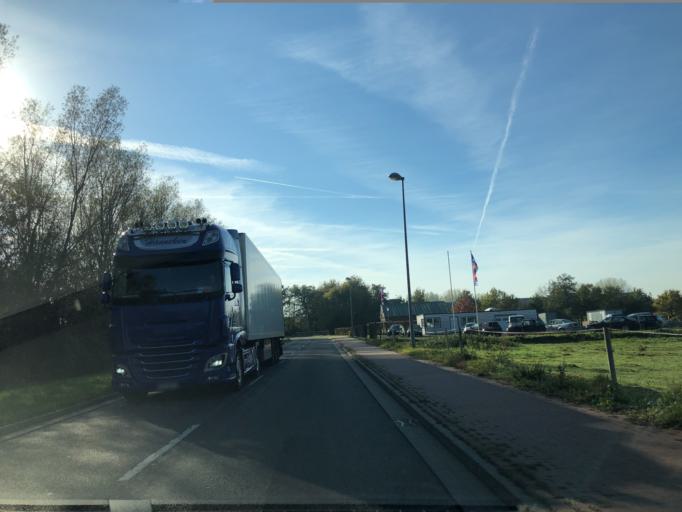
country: DE
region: Lower Saxony
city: Lehe
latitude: 53.0466
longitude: 7.3256
